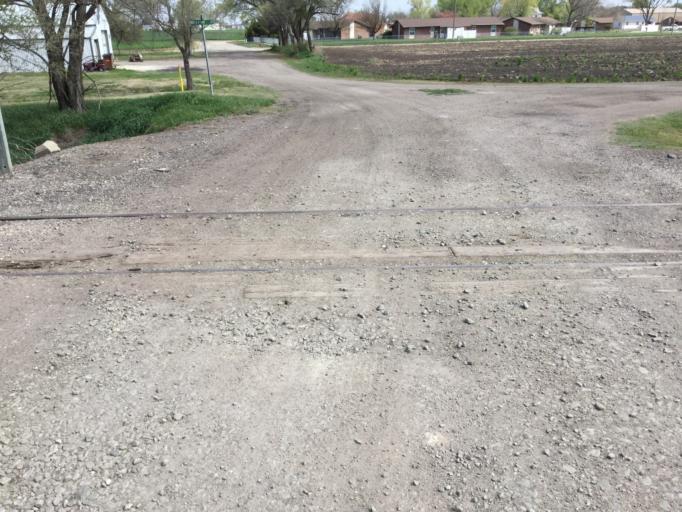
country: US
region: Kansas
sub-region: Osborne County
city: Osborne
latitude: 39.5029
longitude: -98.5531
